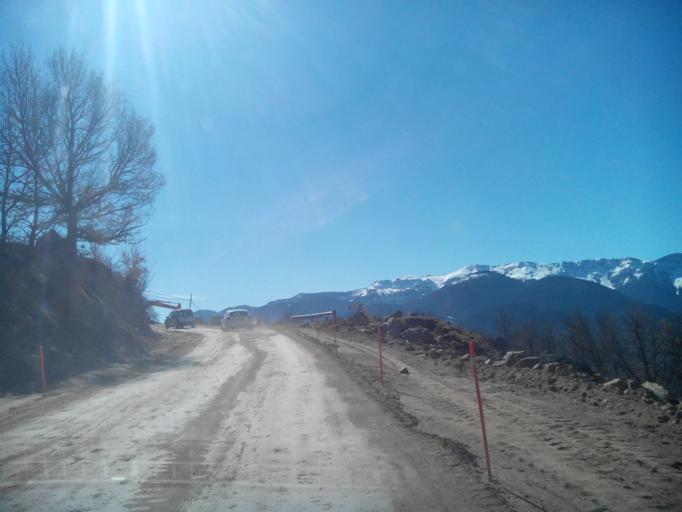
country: ES
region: Catalonia
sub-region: Provincia de Lleida
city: Lles de Cerdanya
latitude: 42.3853
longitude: 1.6843
